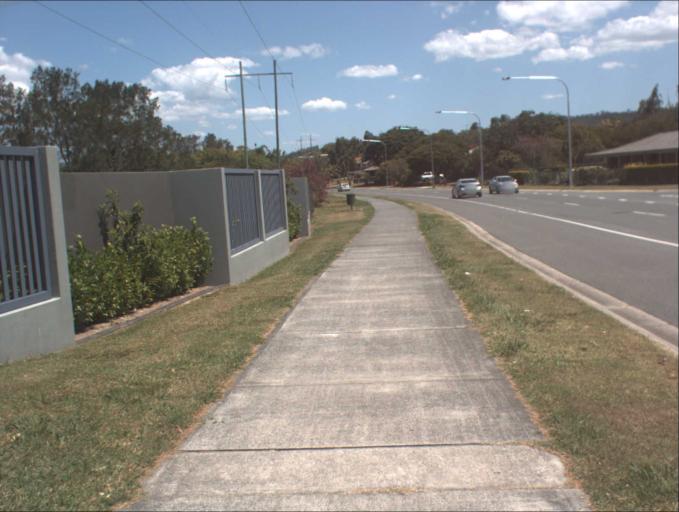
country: AU
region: Queensland
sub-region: Logan
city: Windaroo
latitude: -27.7435
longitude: 153.1927
